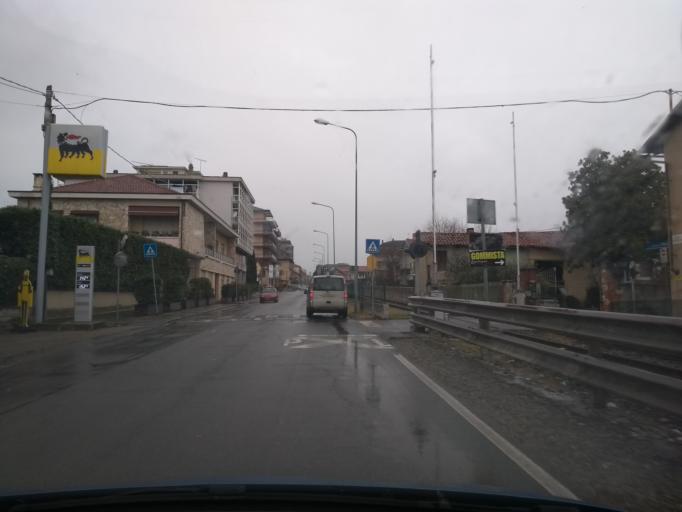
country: IT
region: Piedmont
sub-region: Provincia di Torino
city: Cuorgne
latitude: 45.3868
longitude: 7.6579
